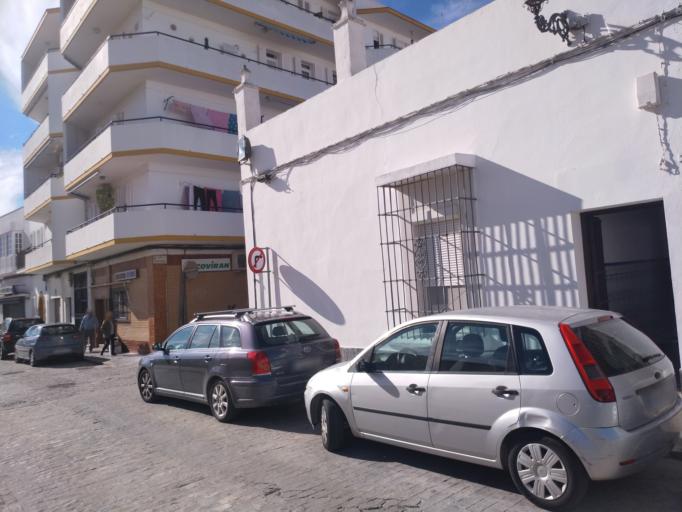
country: ES
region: Andalusia
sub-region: Provincia de Cadiz
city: San Fernando
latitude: 36.4683
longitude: -6.1924
